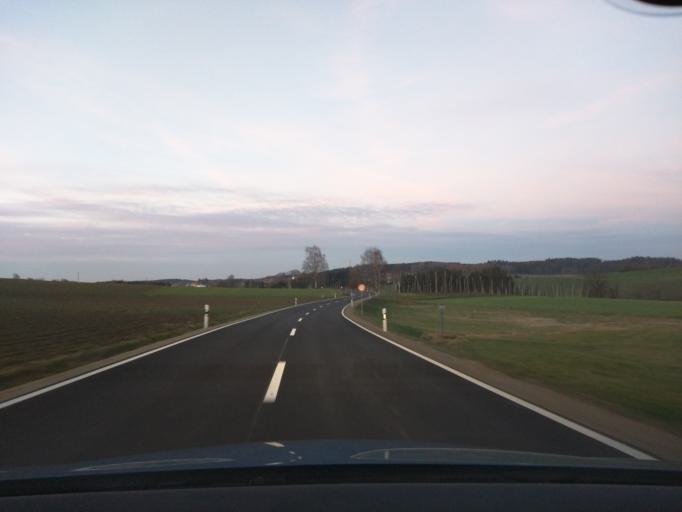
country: DE
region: Bavaria
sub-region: Upper Bavaria
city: Wolfersdorf
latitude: 48.5463
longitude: 11.7516
